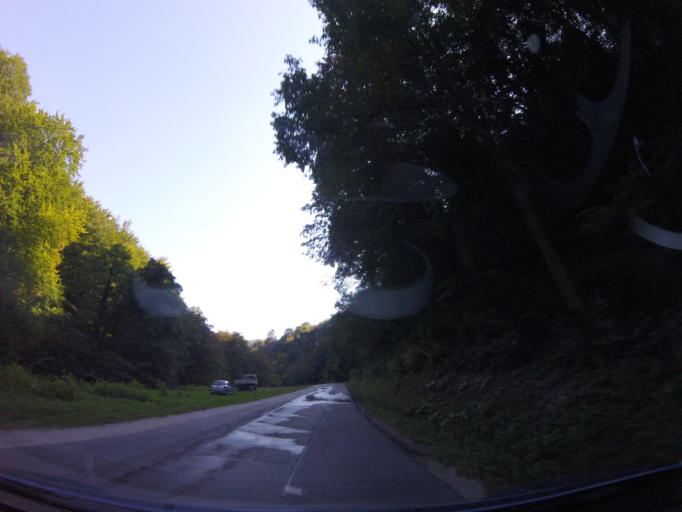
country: HR
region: Zagrebacka
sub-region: Grad Samobor
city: Samobor
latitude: 45.7913
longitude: 15.6921
